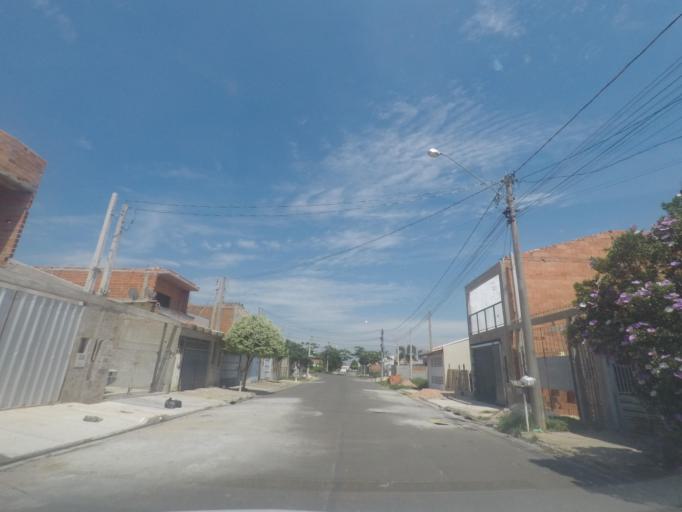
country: BR
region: Sao Paulo
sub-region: Sumare
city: Sumare
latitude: -22.8023
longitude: -47.2650
